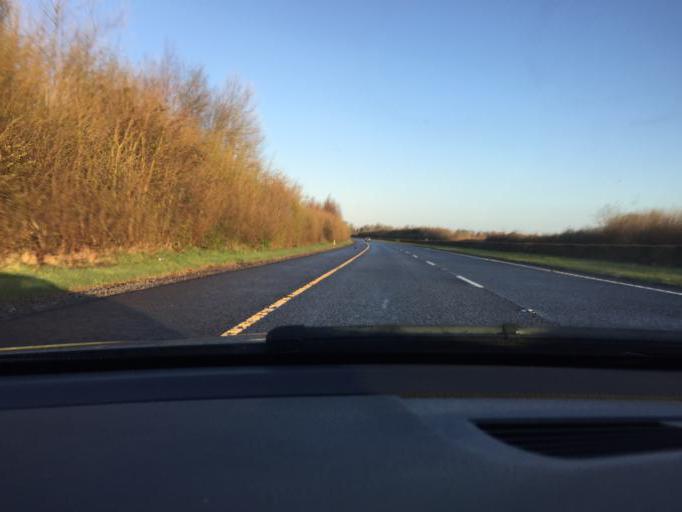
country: IE
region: Leinster
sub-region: An Mhi
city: Stamullin
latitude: 53.6545
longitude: -6.2939
